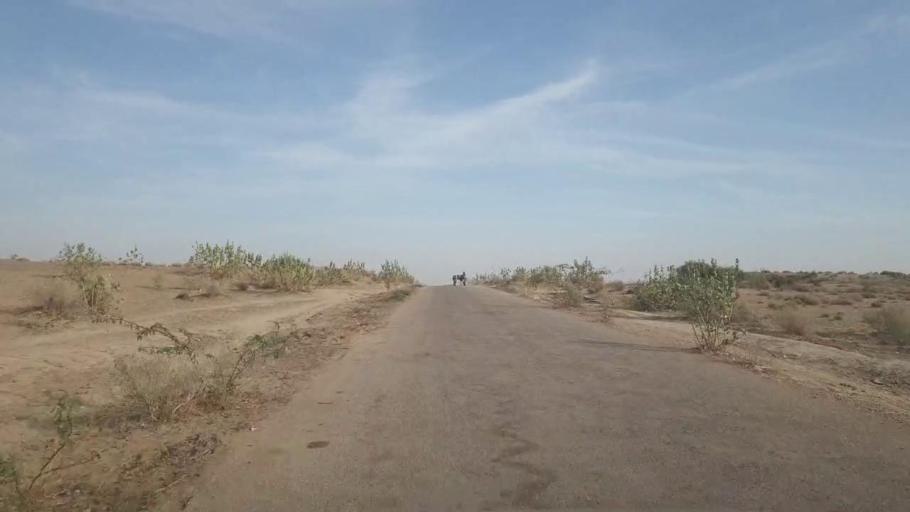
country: PK
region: Sindh
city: Nabisar
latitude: 25.0651
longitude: 69.6523
